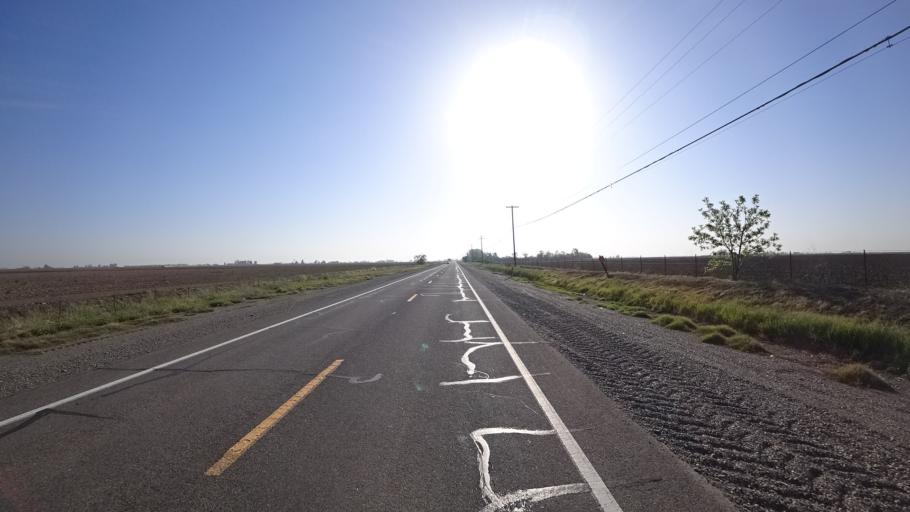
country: US
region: California
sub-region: Glenn County
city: Willows
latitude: 39.5241
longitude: -122.1585
